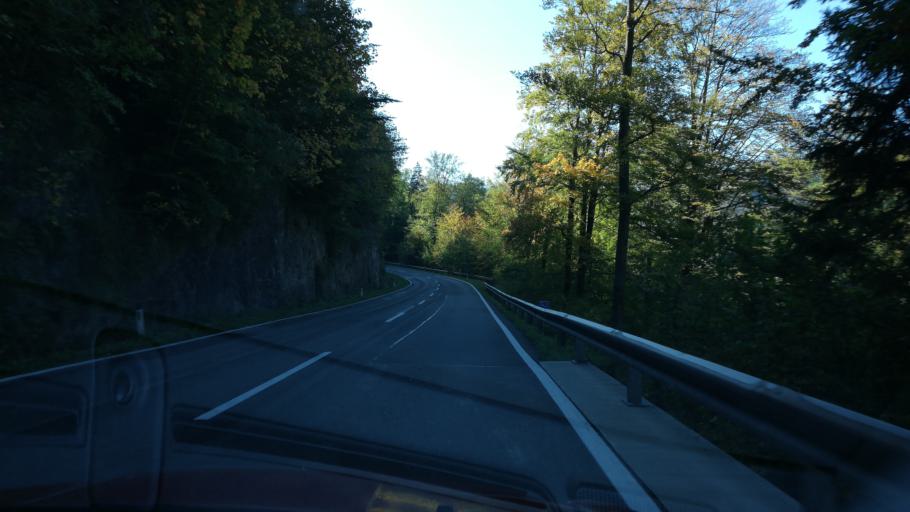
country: AT
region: Styria
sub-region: Politischer Bezirk Liezen
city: Altenmarkt bei Sankt Gallen
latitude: 47.7638
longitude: 14.6470
